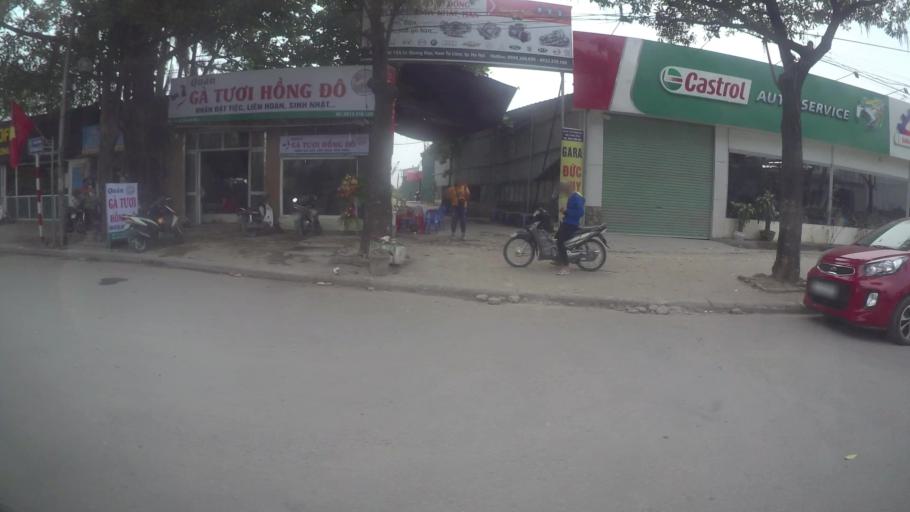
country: VN
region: Ha Noi
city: Cau Dien
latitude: 21.0112
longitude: 105.7716
